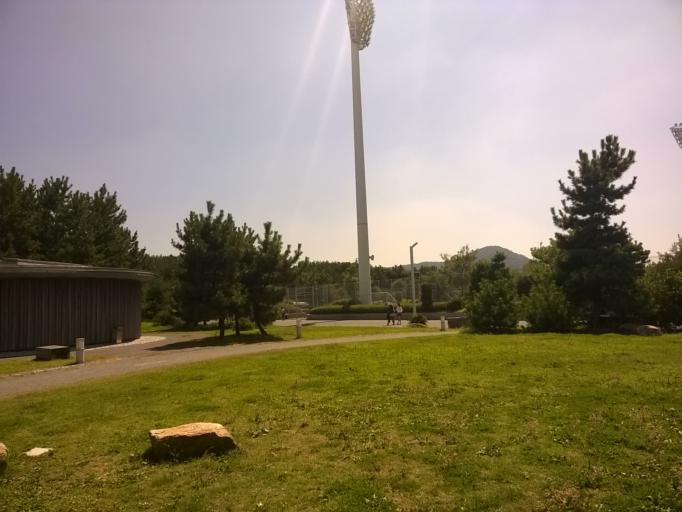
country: JP
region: Yamaguchi
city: Ogori-shimogo
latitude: 34.0043
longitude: 131.3700
